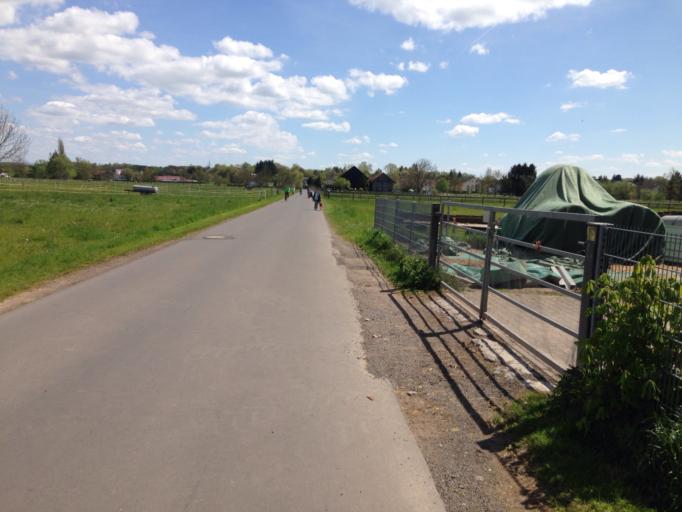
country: DE
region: Hesse
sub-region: Regierungsbezirk Giessen
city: Lich
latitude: 50.5180
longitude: 8.8241
